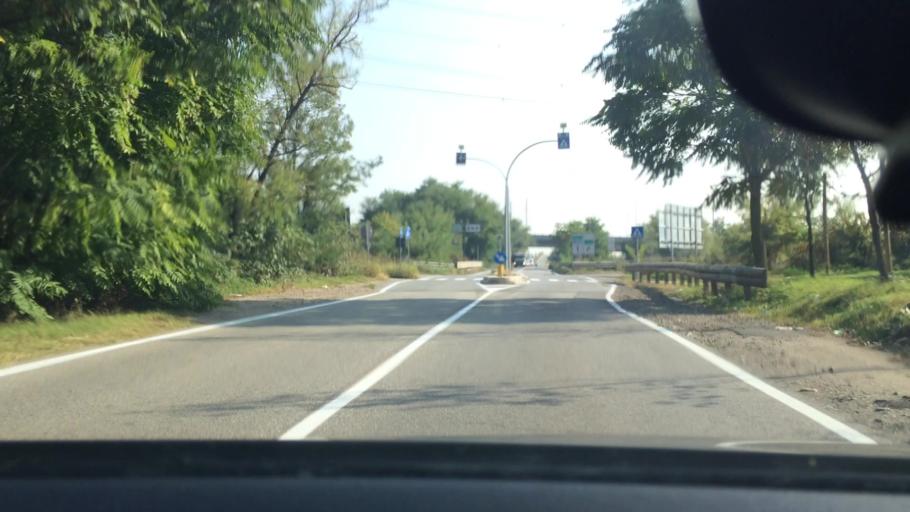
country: IT
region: Lombardy
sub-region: Citta metropolitana di Milano
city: Rho
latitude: 45.5169
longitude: 9.0537
